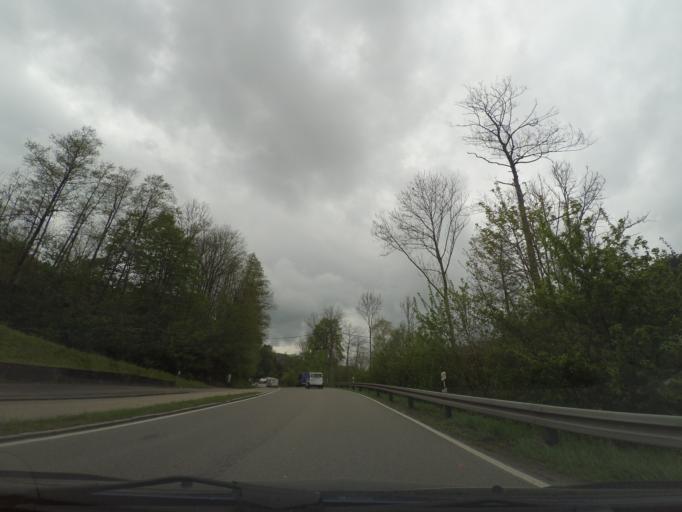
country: DE
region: Baden-Wuerttemberg
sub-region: Regierungsbezirk Stuttgart
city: Murrhardt
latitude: 48.9759
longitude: 9.5978
